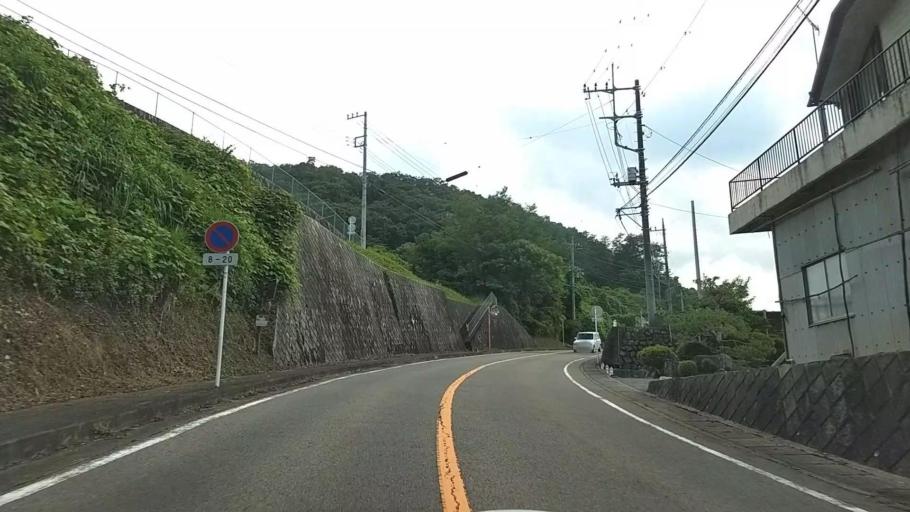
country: JP
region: Yamanashi
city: Uenohara
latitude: 35.6153
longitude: 139.1371
